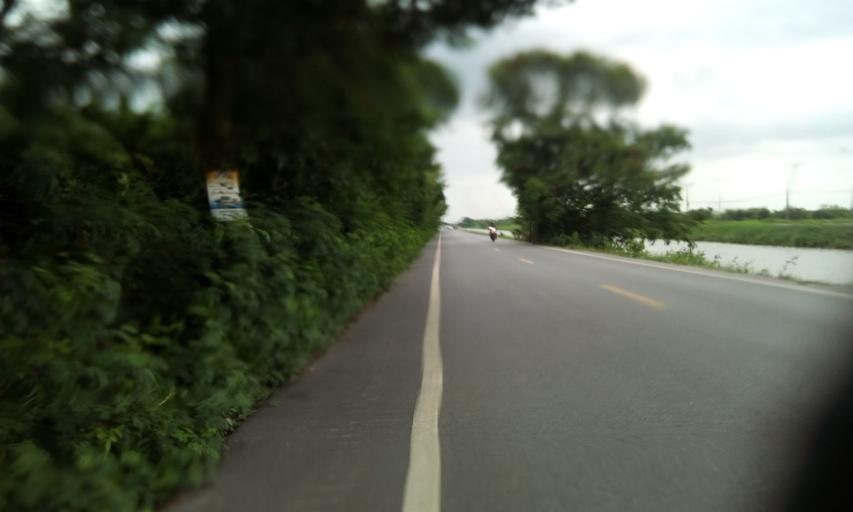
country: TH
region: Pathum Thani
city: Nong Suea
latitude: 14.0716
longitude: 100.8467
